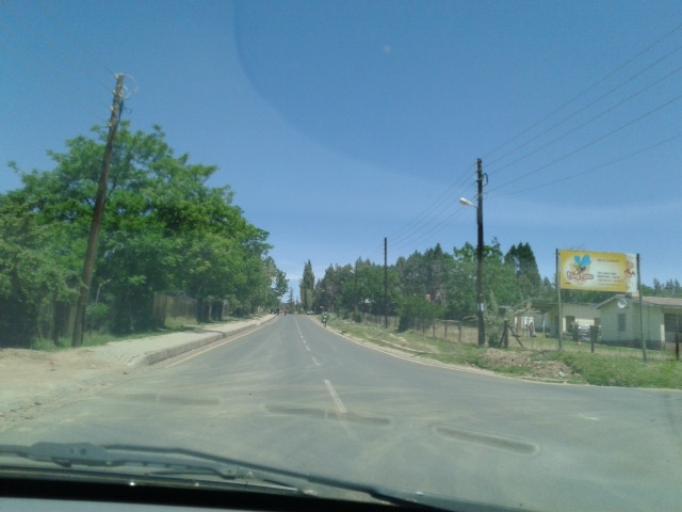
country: LS
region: Maseru
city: Maseru
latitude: -29.3030
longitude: 27.4796
